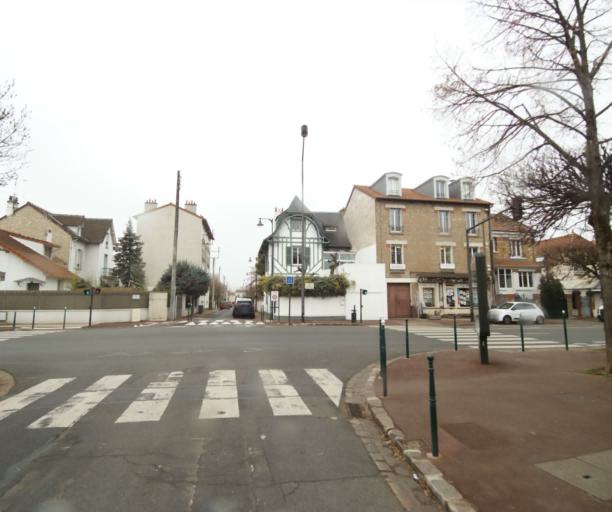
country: FR
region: Ile-de-France
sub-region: Departement des Hauts-de-Seine
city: Rueil-Malmaison
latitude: 48.8843
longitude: 2.1786
